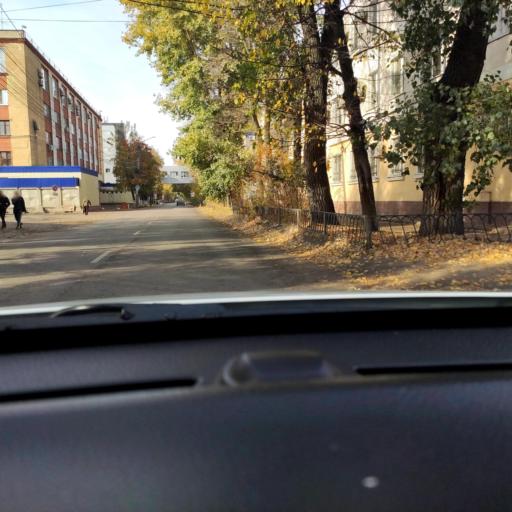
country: RU
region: Voronezj
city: Voronezh
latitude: 51.6852
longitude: 39.1781
